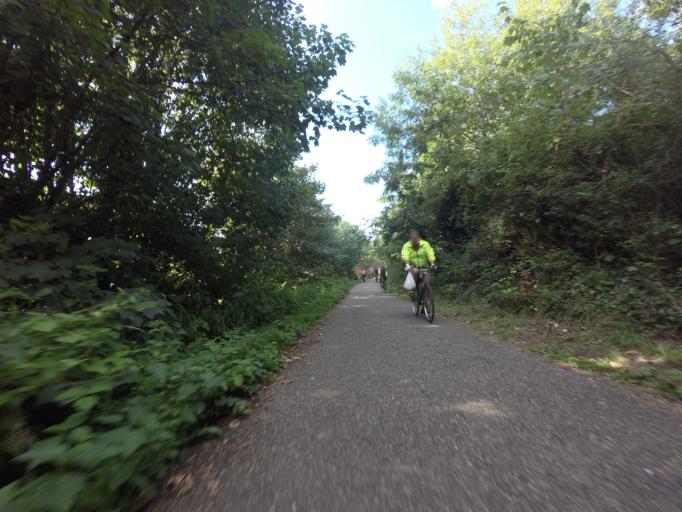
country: GB
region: England
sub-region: East Sussex
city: Hailsham
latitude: 50.8627
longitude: 0.2565
